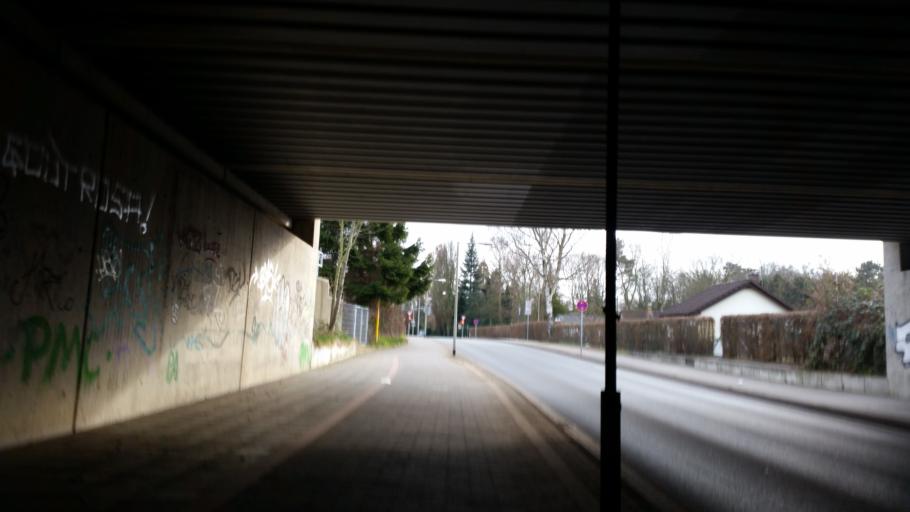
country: DE
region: Lower Saxony
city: Hannover
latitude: 52.3972
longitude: 9.7015
